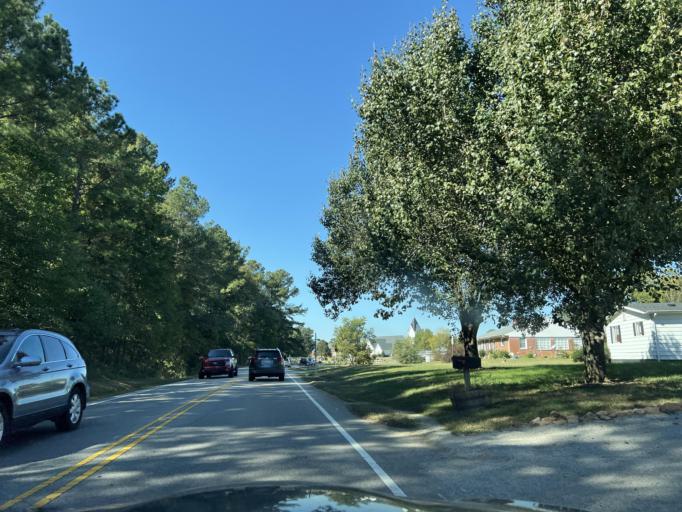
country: US
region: North Carolina
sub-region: Johnston County
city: Clayton
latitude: 35.6831
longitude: -78.5247
